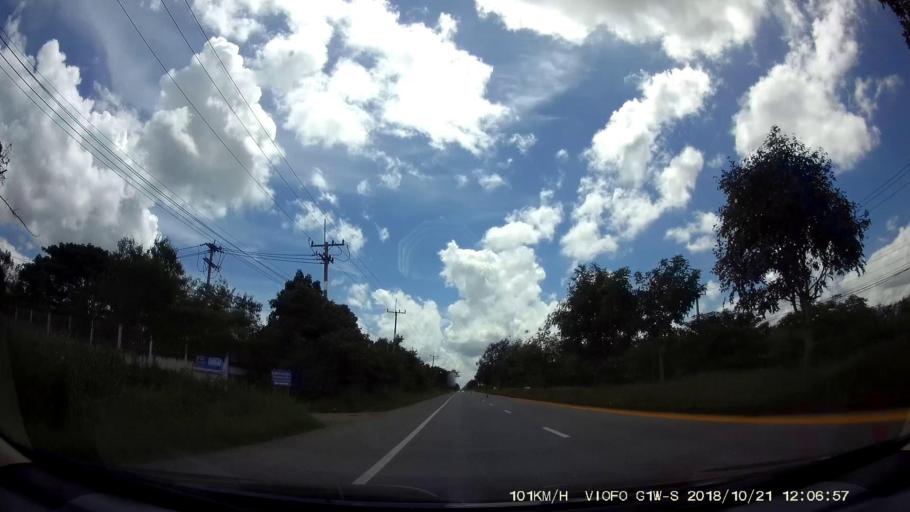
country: TH
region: Chaiyaphum
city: Chatturat
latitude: 15.4550
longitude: 101.8273
